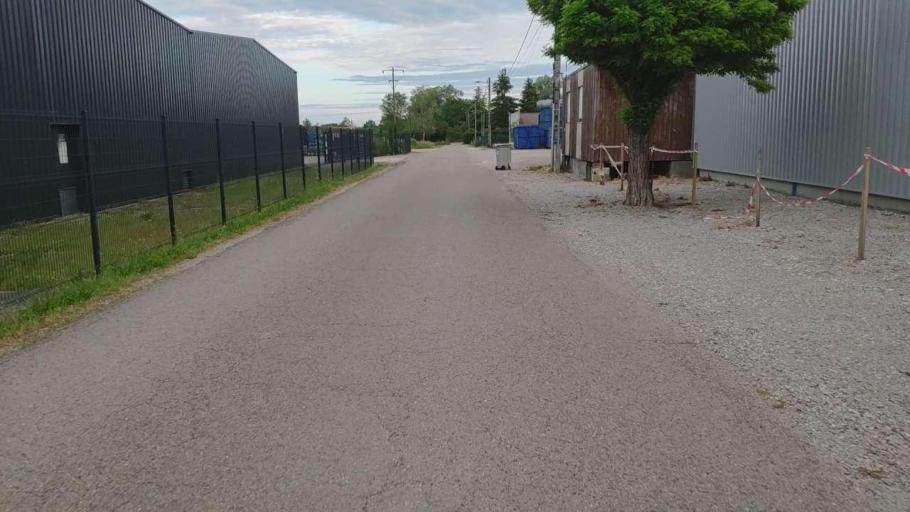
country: FR
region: Franche-Comte
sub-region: Departement du Jura
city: Bletterans
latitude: 46.7501
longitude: 5.4689
